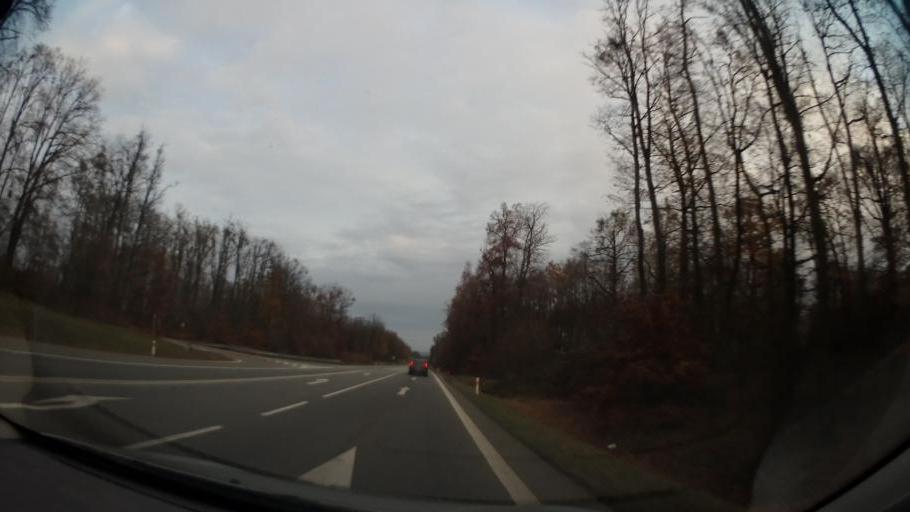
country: CZ
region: South Moravian
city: Ricany
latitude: 49.1909
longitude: 16.4487
